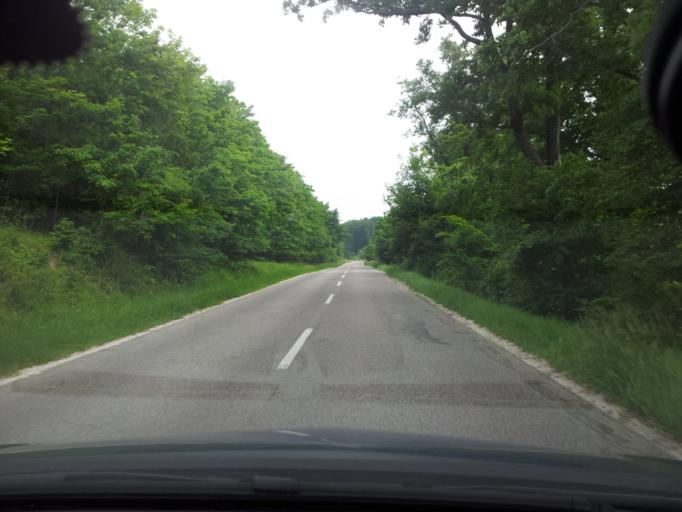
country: SK
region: Nitriansky
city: Partizanske
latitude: 48.5421
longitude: 18.4428
